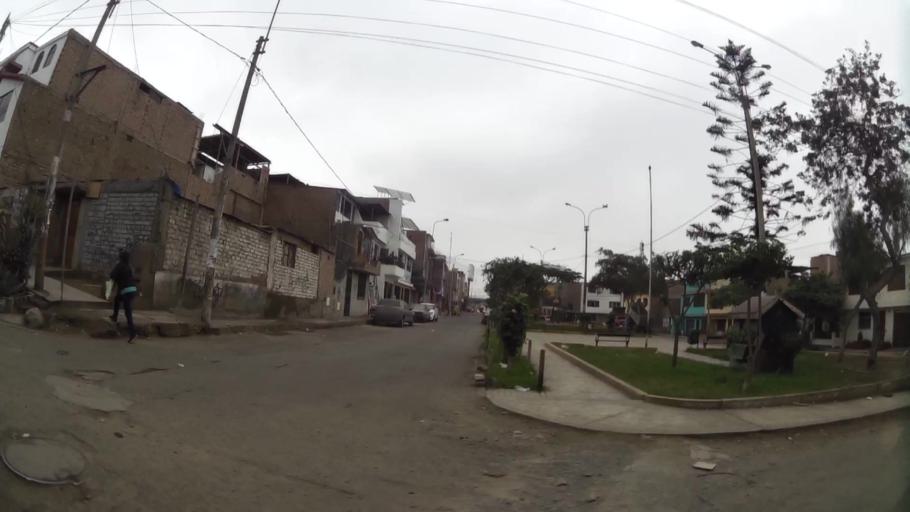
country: PE
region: Lima
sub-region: Lima
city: Surco
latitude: -12.1483
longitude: -76.9797
